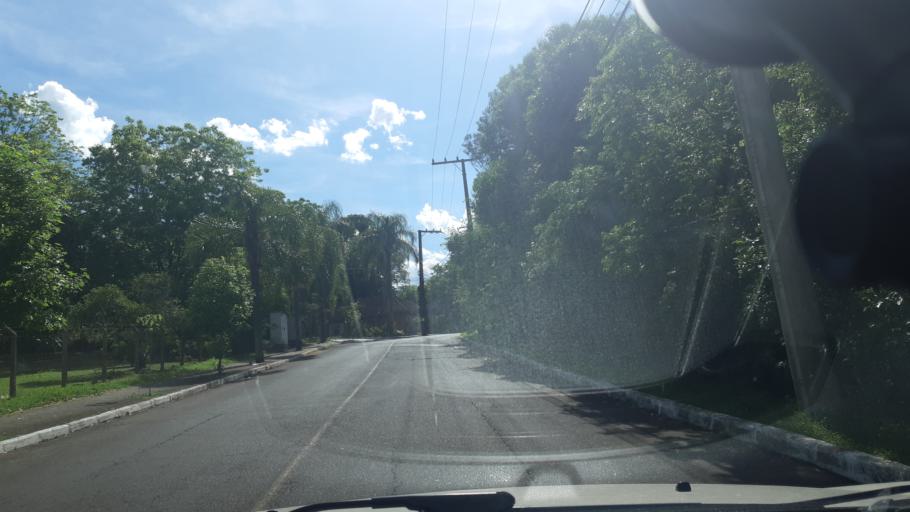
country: BR
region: Rio Grande do Sul
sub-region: Ivoti
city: Ivoti
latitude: -29.6192
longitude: -51.1200
